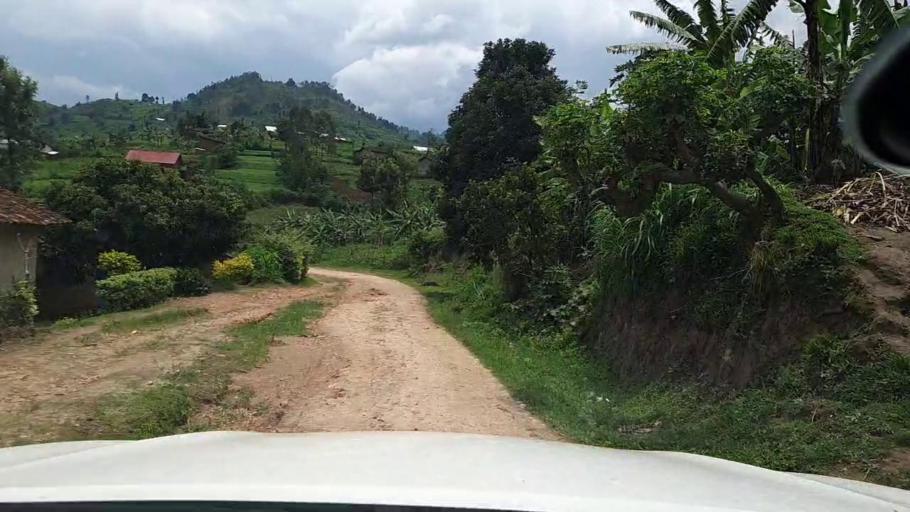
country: RW
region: Western Province
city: Kibuye
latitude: -2.0818
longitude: 29.4199
